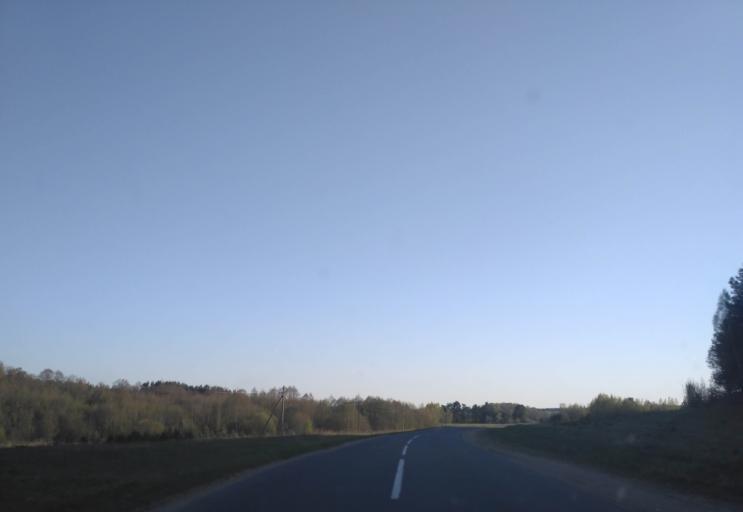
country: BY
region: Minsk
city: Radashkovichy
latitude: 54.1481
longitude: 27.2157
